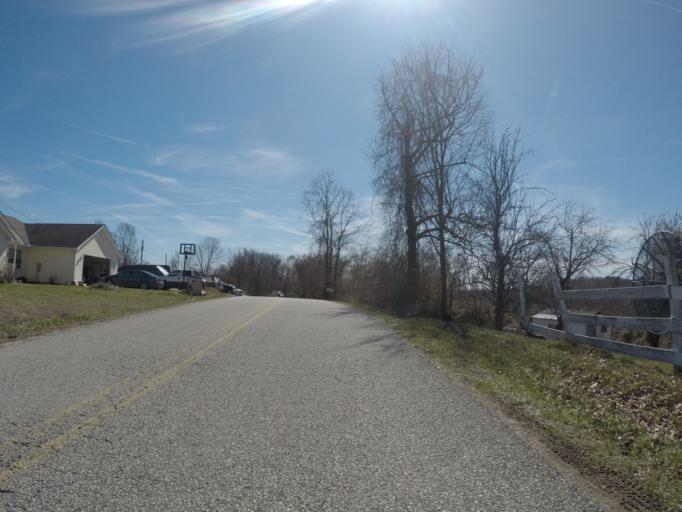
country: US
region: West Virginia
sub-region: Cabell County
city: Huntington
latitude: 38.4522
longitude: -82.4928
